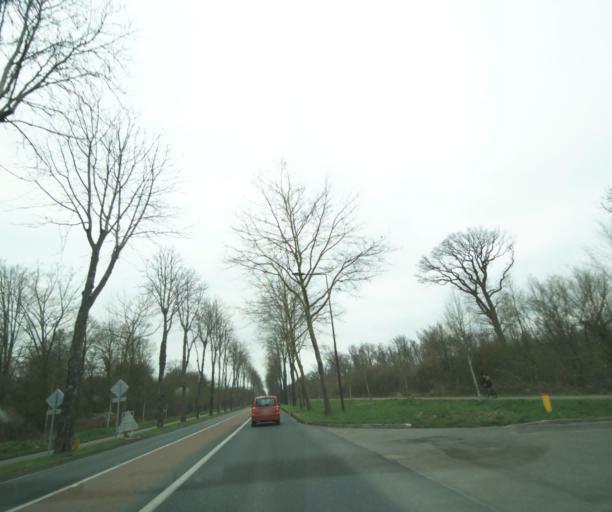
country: FR
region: Ile-de-France
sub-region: Departement des Yvelines
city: Saint-Germain-en-Laye
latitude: 48.9119
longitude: 2.0719
